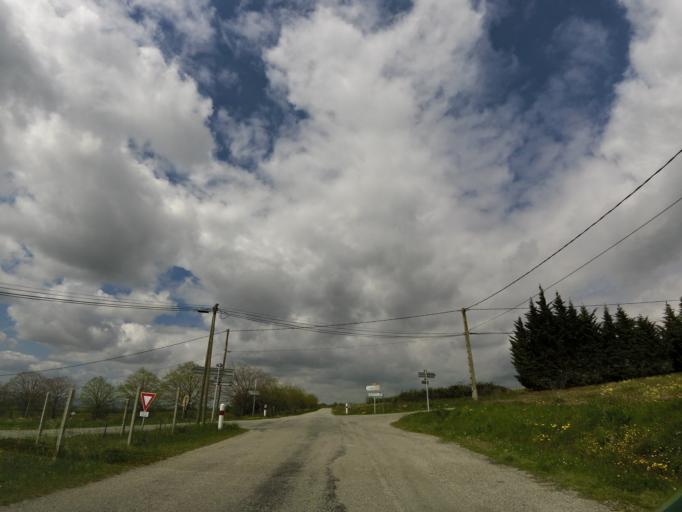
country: FR
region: Languedoc-Roussillon
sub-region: Departement de l'Aude
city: Villepinte
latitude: 43.3538
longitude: 2.1064
